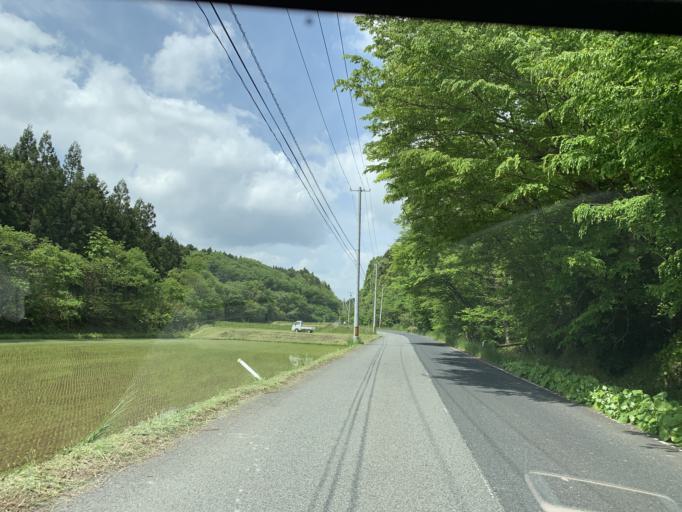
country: JP
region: Miyagi
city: Furukawa
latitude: 38.7726
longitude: 140.9600
